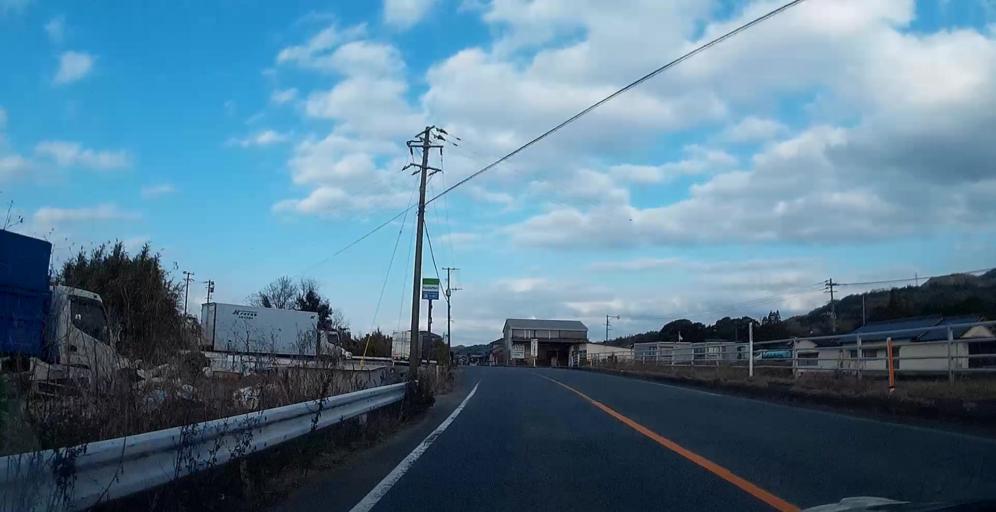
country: JP
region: Kumamoto
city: Yatsushiro
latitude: 32.5372
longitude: 130.6700
